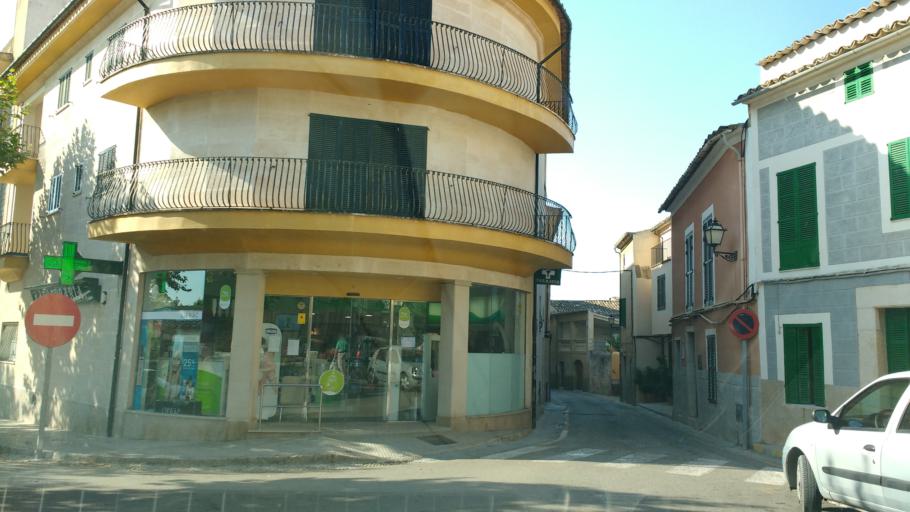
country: ES
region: Balearic Islands
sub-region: Illes Balears
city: Alaro
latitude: 39.7053
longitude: 2.7906
